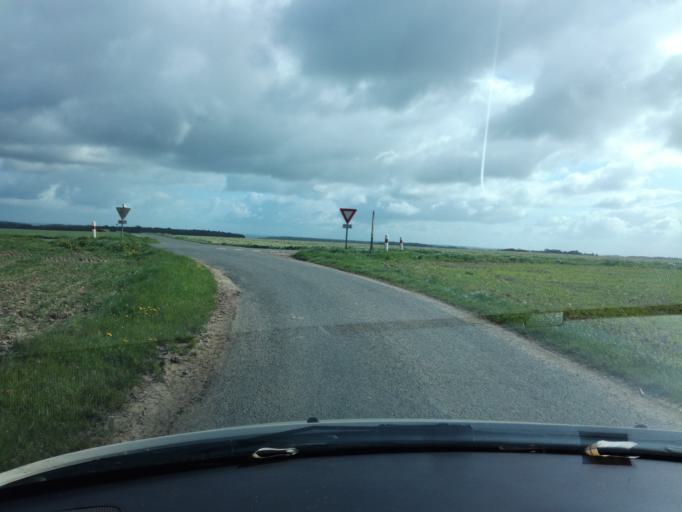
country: FR
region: Picardie
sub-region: Departement de la Somme
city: Hornoy-le-Bourg
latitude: 49.8566
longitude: 1.8539
